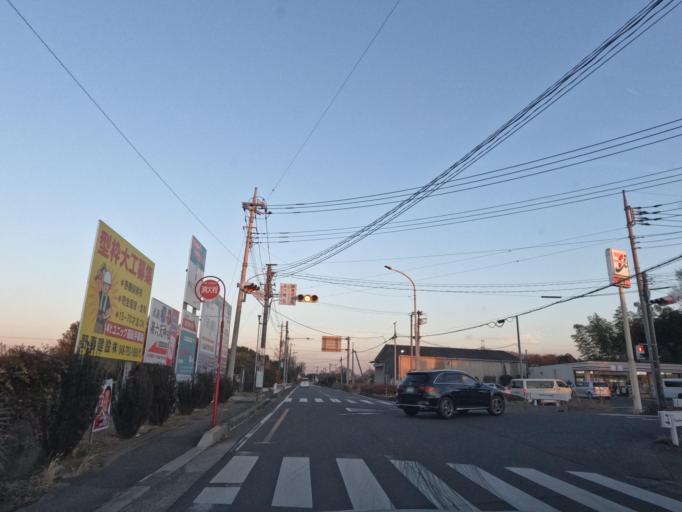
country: JP
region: Saitama
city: Kasukabe
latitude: 35.9298
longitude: 139.7390
